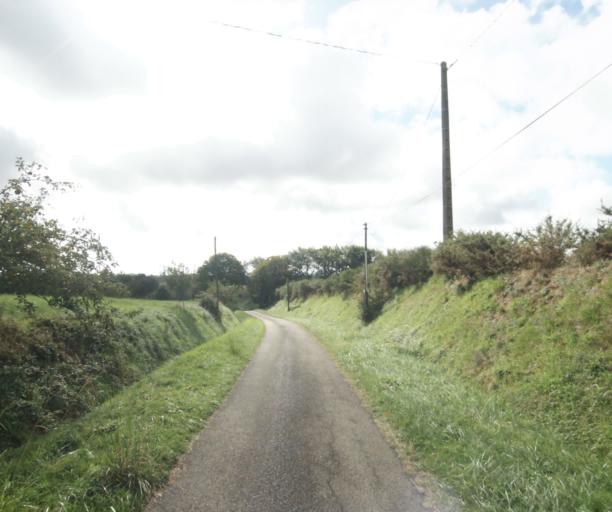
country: FR
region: Midi-Pyrenees
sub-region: Departement du Gers
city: Nogaro
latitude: 43.8353
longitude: -0.0932
